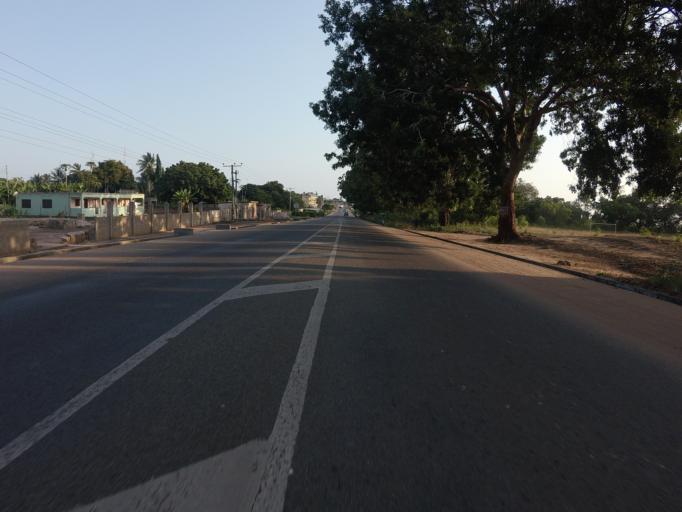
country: GH
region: Volta
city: Anloga
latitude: 6.0082
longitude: 0.5961
